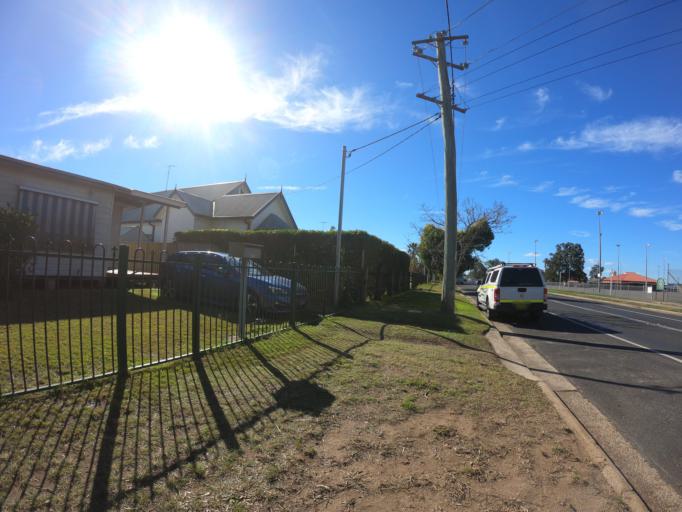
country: AU
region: New South Wales
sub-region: Hawkesbury
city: South Windsor
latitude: -33.6246
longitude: 150.8029
